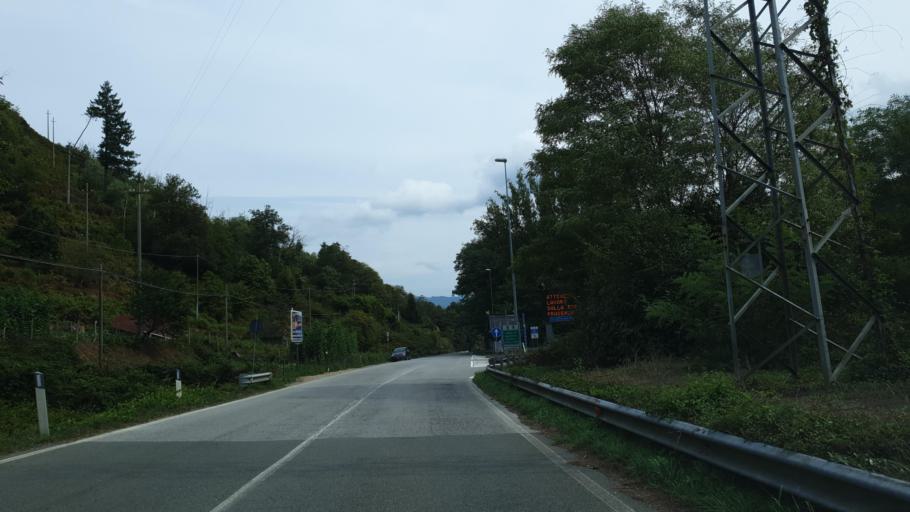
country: IT
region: Liguria
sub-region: Provincia di La Spezia
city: Carrodano
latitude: 44.2382
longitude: 9.6472
